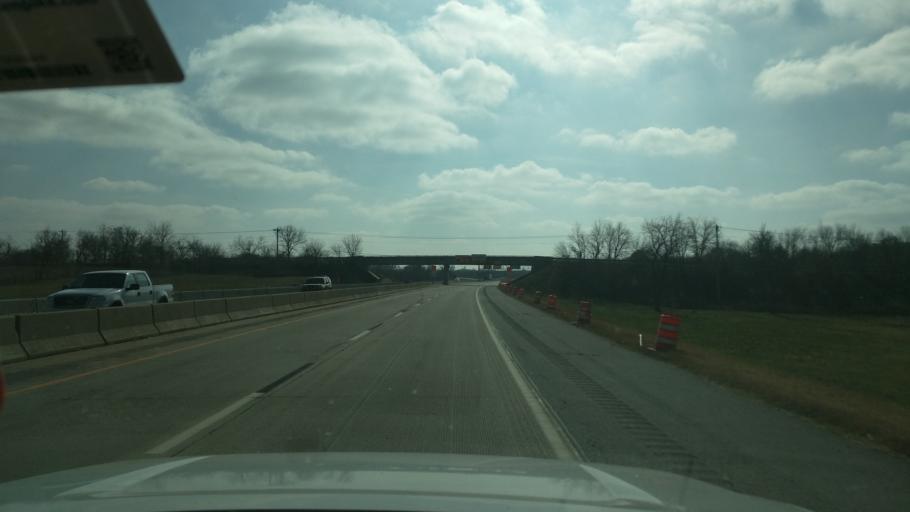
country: US
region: Oklahoma
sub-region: Wagoner County
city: Coweta
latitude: 35.9608
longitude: -95.5904
